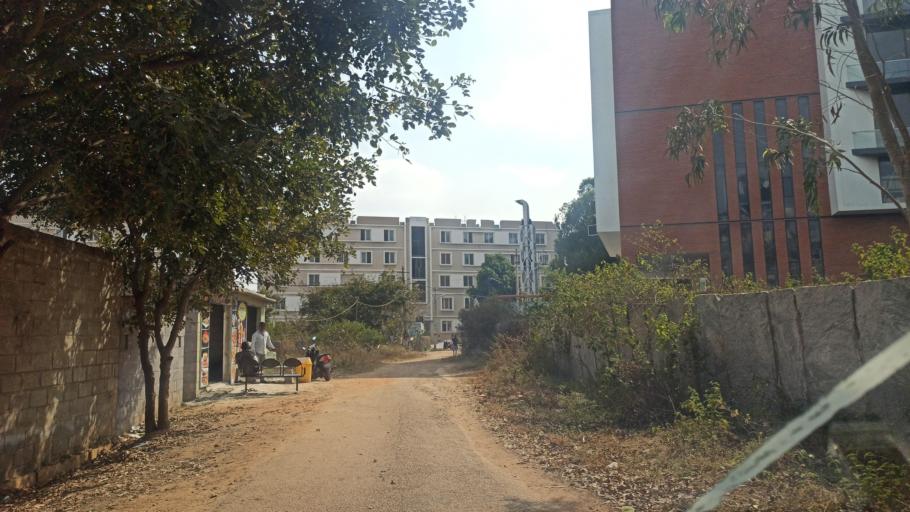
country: IN
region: Karnataka
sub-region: Bangalore Urban
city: Yelahanka
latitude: 13.1155
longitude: 77.6089
